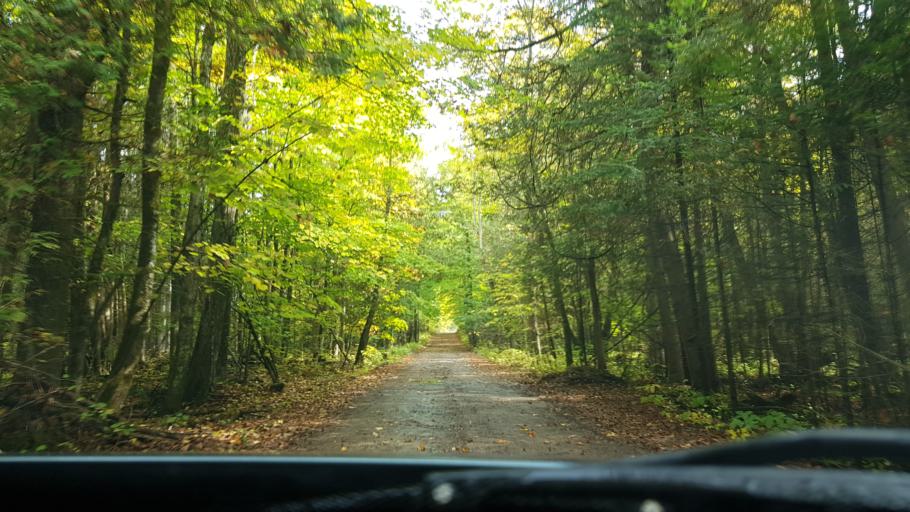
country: CA
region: Ontario
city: Orillia
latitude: 44.6866
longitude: -79.0452
